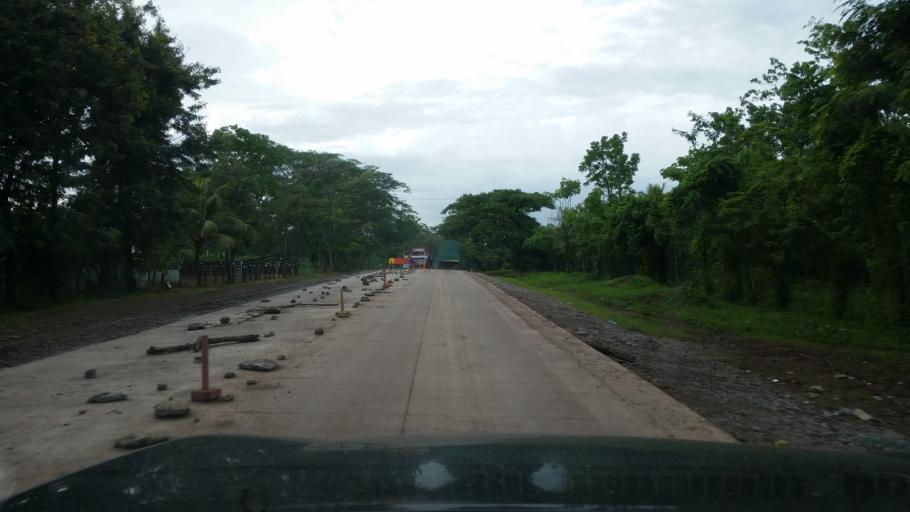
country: NI
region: Matagalpa
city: Rio Blanco
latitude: 13.2046
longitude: -84.9492
